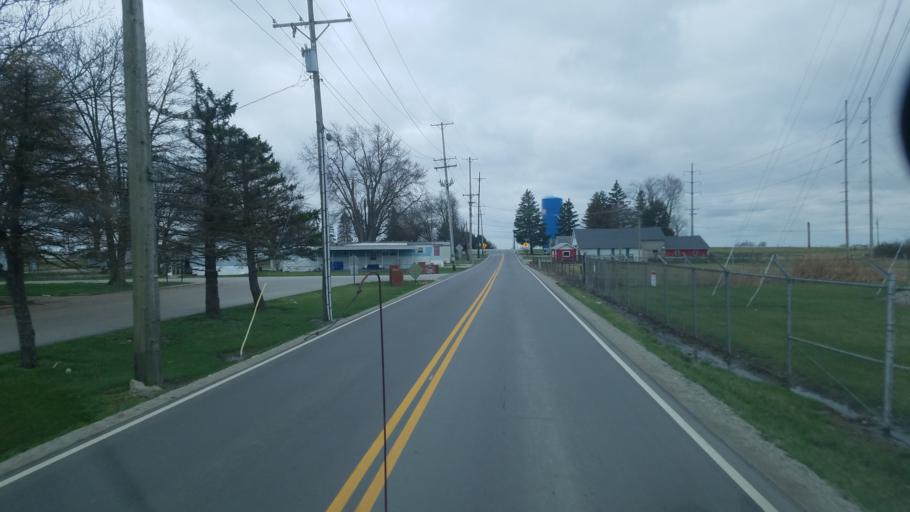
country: US
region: Ohio
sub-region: Fayette County
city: Washington Court House
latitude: 39.5295
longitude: -83.4711
